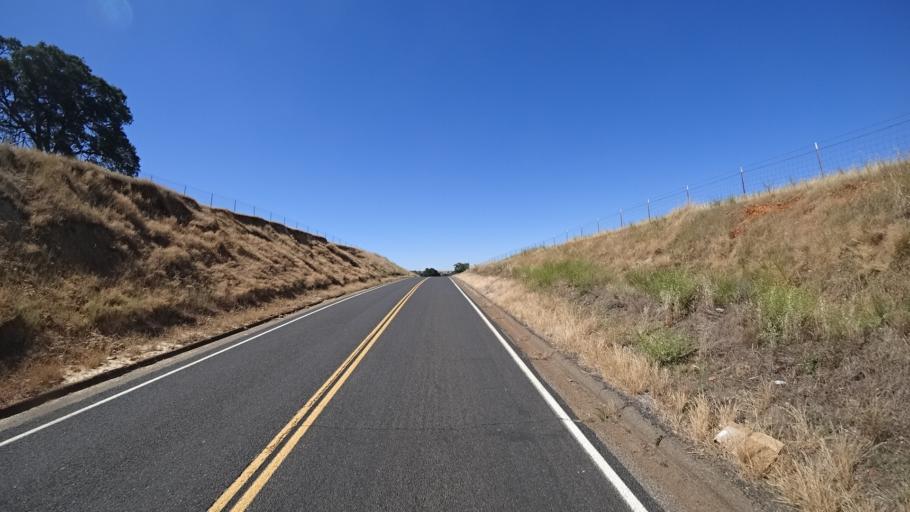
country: US
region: California
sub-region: Calaveras County
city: Rancho Calaveras
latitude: 38.0899
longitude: -120.8731
